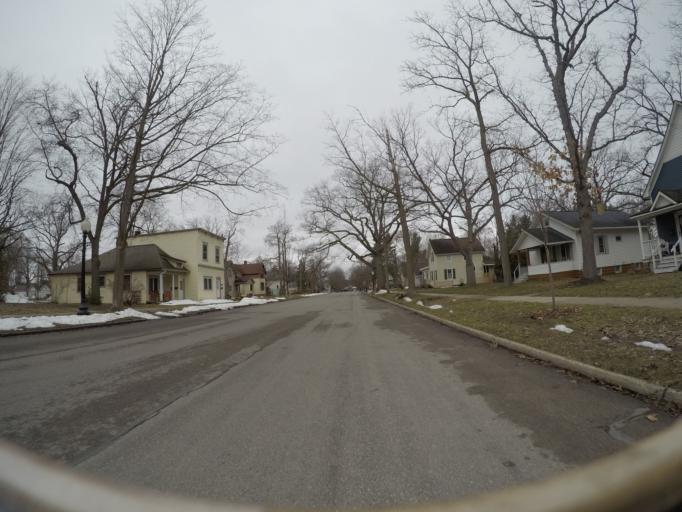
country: US
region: Michigan
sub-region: Grand Traverse County
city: Traverse City
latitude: 44.7605
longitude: -85.6041
